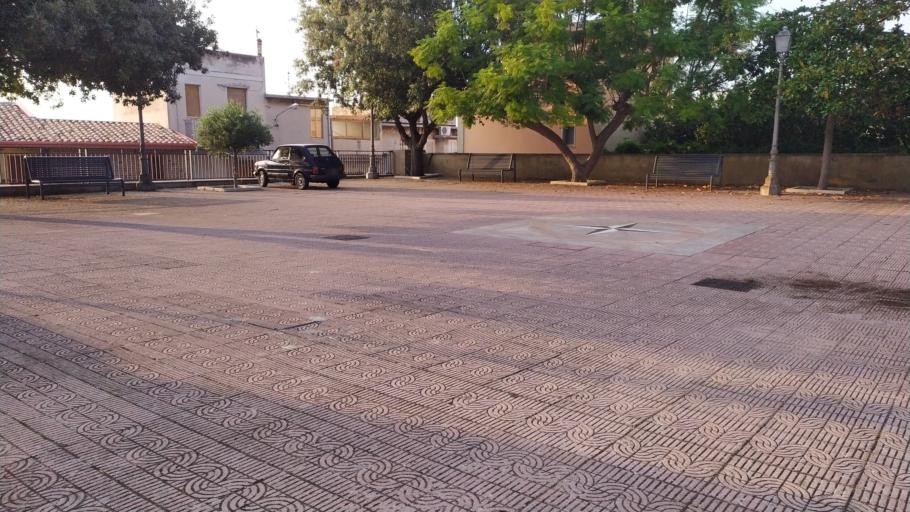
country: IT
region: Sicily
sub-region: Messina
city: San Pier Niceto
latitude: 38.1621
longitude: 15.3471
